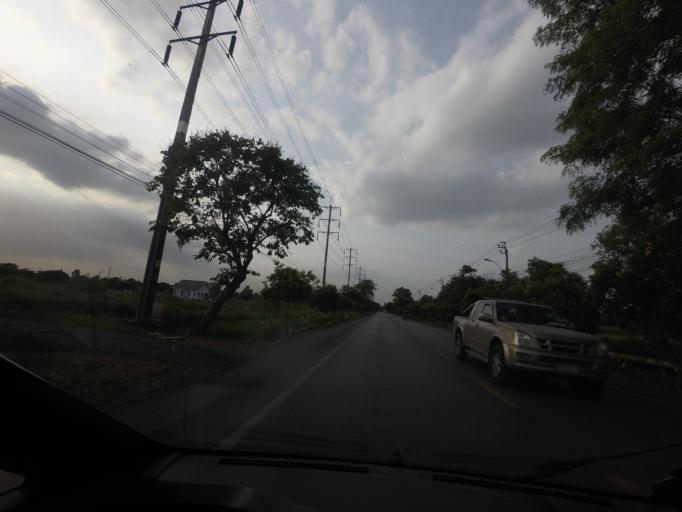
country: TH
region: Bangkok
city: Nong Chok
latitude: 13.8813
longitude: 100.8638
